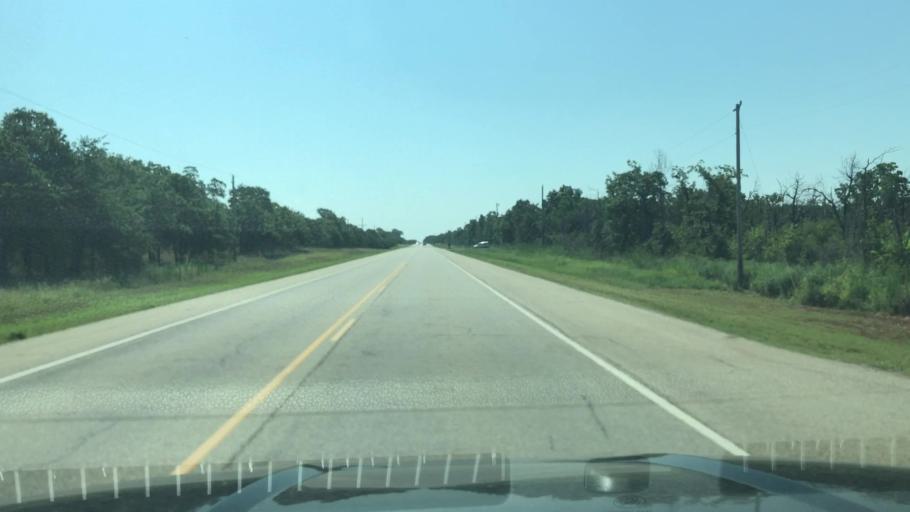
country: US
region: Oklahoma
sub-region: Creek County
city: Mannford
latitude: 35.9956
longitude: -96.3591
